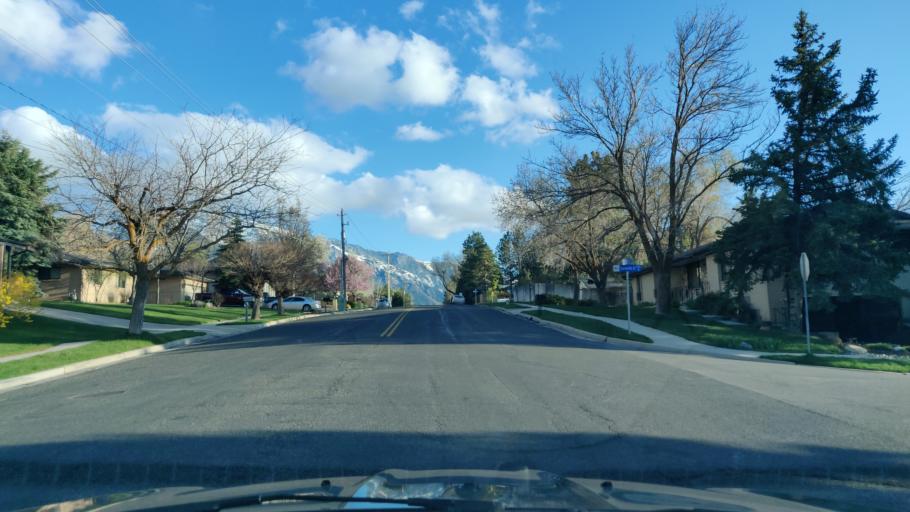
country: US
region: Utah
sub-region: Salt Lake County
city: Cottonwood Heights
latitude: 40.6141
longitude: -111.7960
